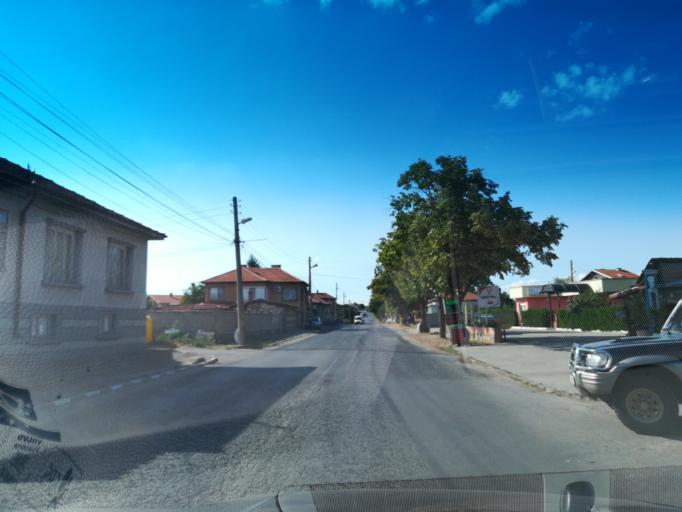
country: BG
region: Khaskovo
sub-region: Obshtina Mineralni Bani
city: Mineralni Bani
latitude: 42.0186
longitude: 25.4170
